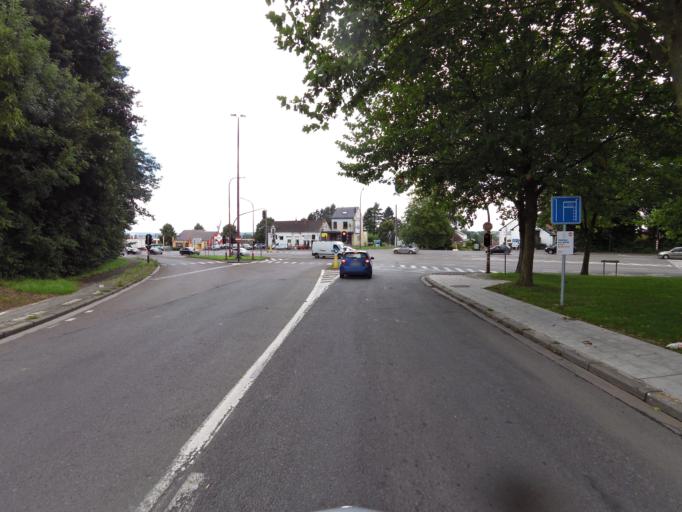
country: BE
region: Wallonia
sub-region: Province du Hainaut
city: Mons
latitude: 50.4515
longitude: 3.9801
